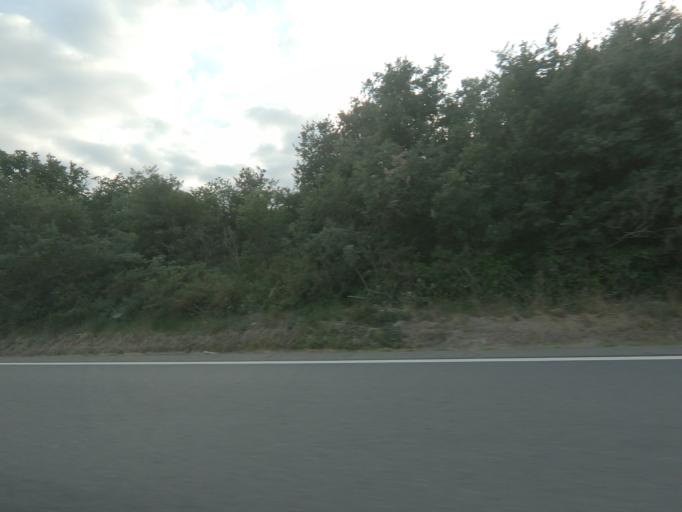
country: ES
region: Galicia
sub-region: Provincia de Ourense
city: Taboadela
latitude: 42.2525
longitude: -7.8358
